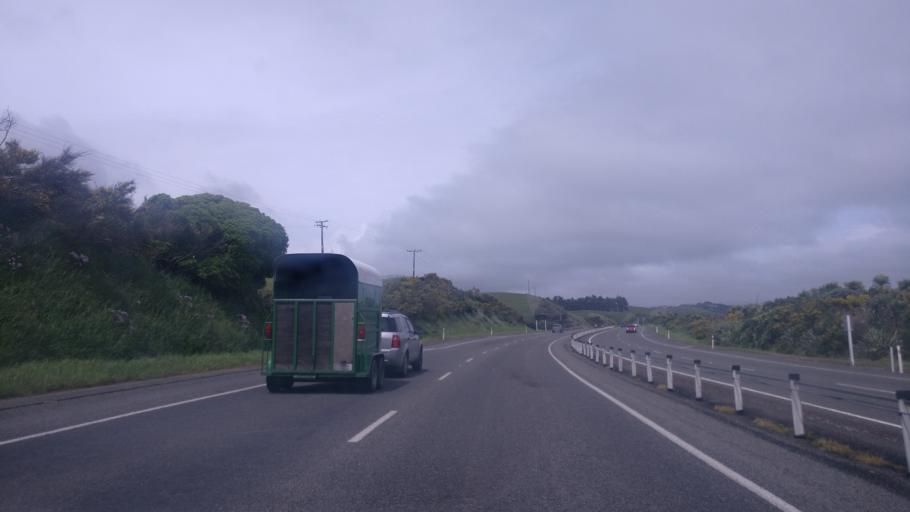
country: NZ
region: Wellington
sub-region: Porirua City
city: Porirua
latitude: -41.0640
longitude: 174.8774
